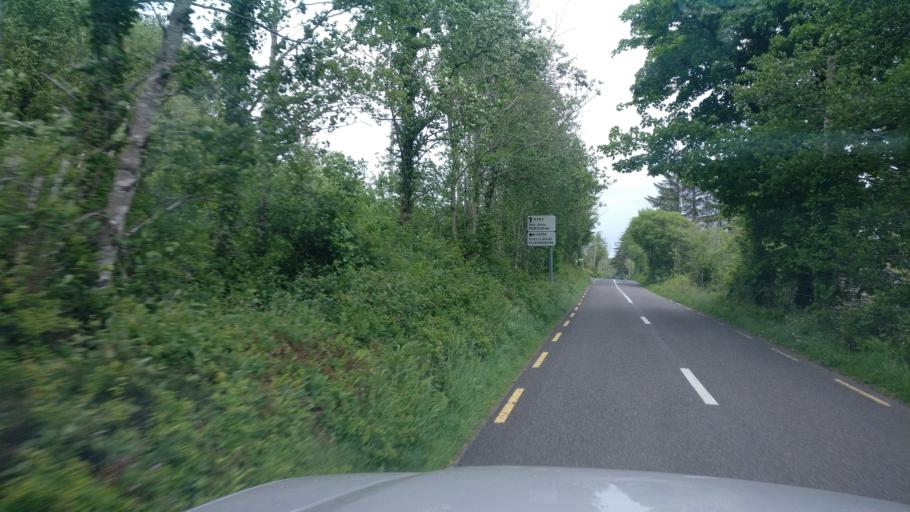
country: IE
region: Connaught
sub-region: County Galway
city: Loughrea
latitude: 53.0720
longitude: -8.5887
